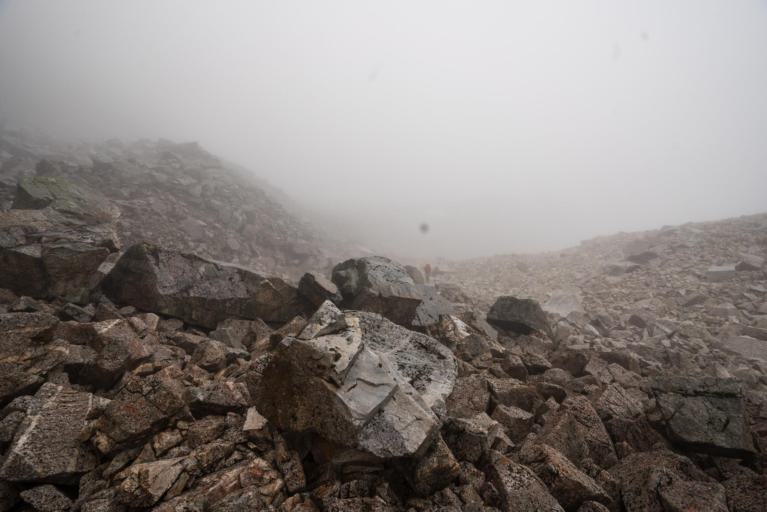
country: RU
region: Transbaikal Territory
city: Chara
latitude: 56.9760
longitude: 117.6531
